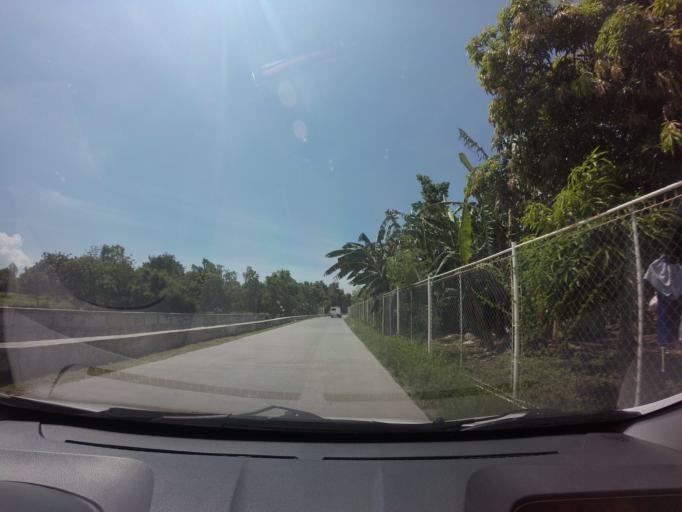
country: PH
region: Calabarzon
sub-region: Province of Rizal
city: Las Pinas
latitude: 14.4241
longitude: 120.9870
